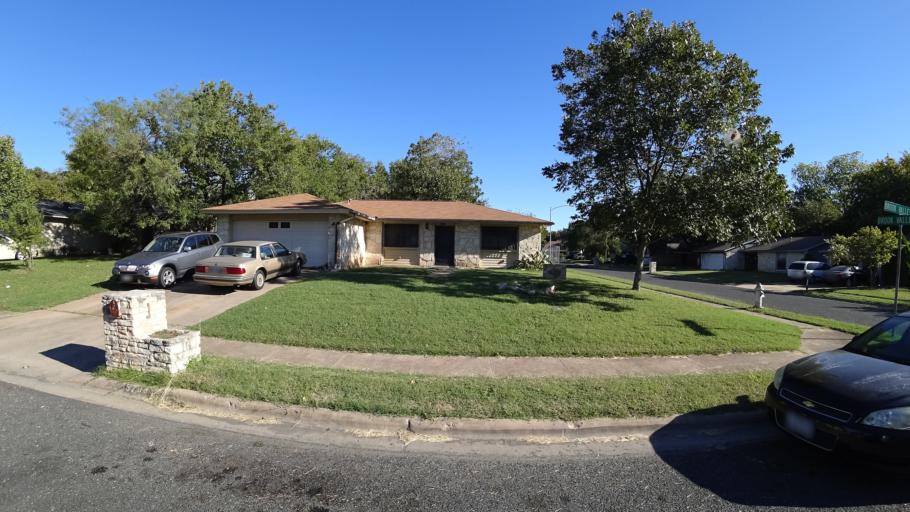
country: US
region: Texas
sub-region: Travis County
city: Hornsby Bend
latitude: 30.3070
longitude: -97.6543
